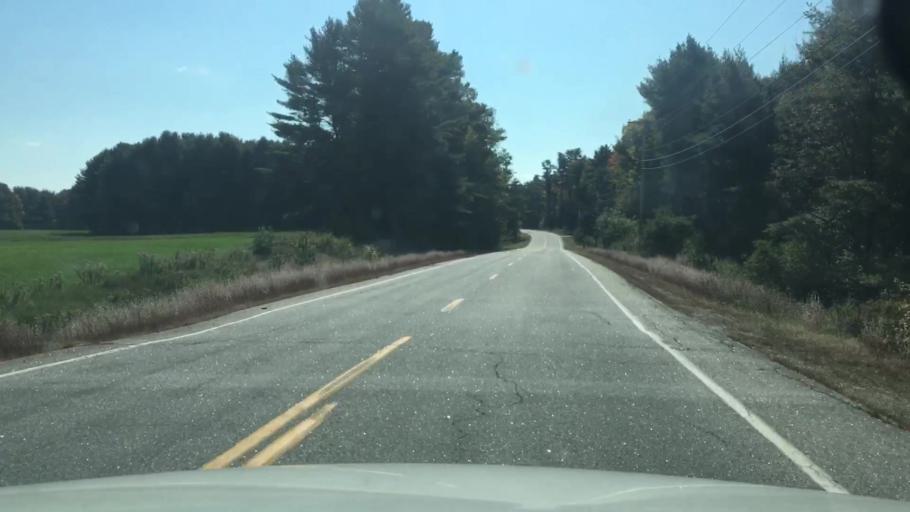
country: US
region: Maine
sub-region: Androscoggin County
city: Lisbon Falls
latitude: 44.0347
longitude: -70.0368
